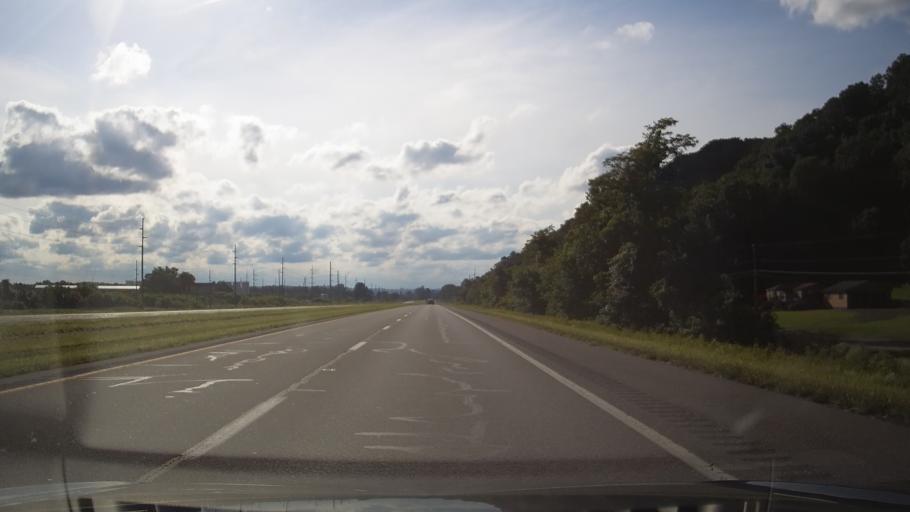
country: US
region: Kentucky
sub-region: Greenup County
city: Greenup
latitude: 38.5762
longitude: -82.7827
